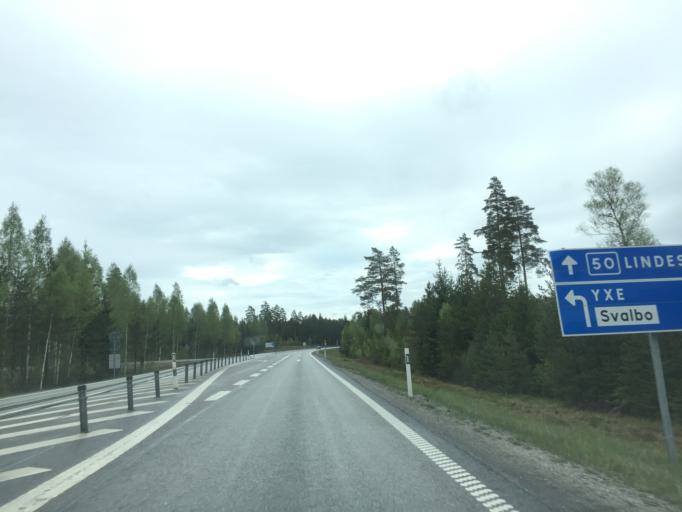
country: SE
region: OErebro
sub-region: Lindesbergs Kommun
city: Lindesberg
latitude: 59.5420
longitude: 15.2062
